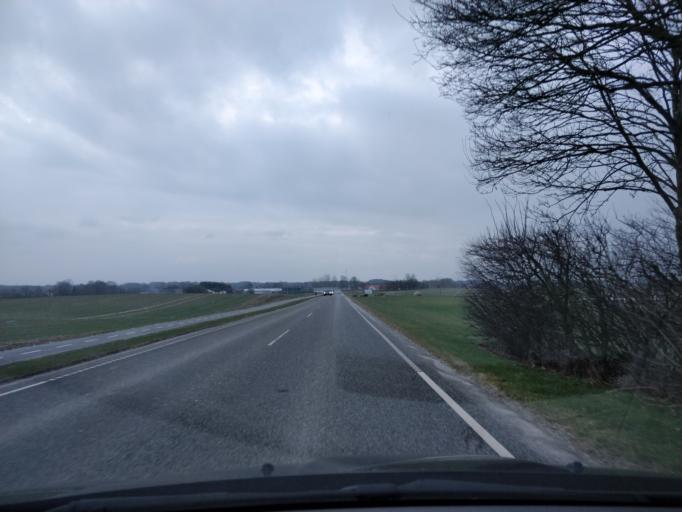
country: DK
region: South Denmark
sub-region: Vejle Kommune
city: Vejle
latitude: 55.7653
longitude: 9.5610
